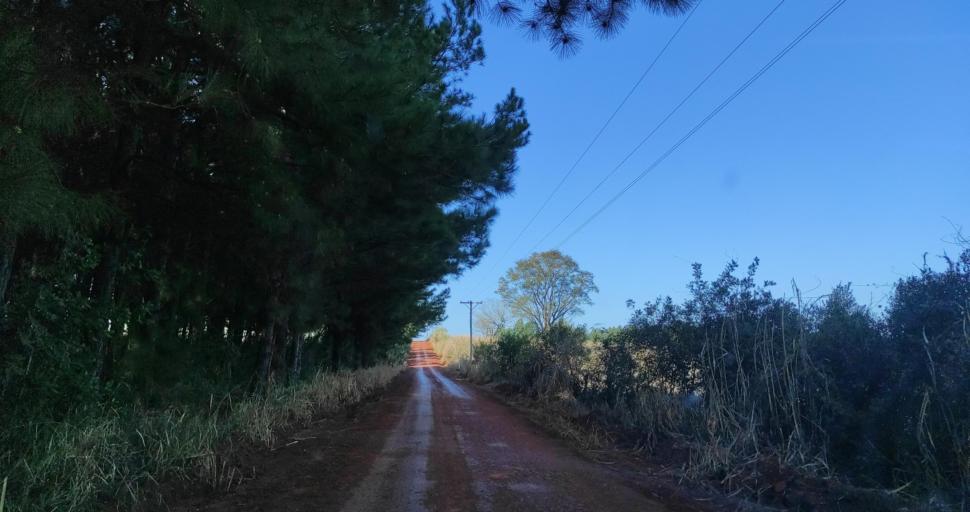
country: AR
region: Misiones
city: Capiovi
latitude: -26.8991
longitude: -55.0498
